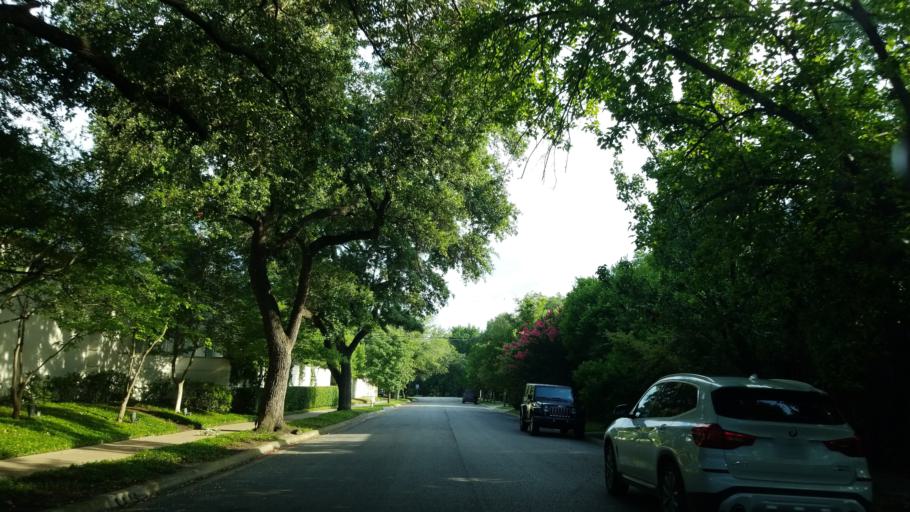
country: US
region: Texas
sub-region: Dallas County
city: Highland Park
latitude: 32.8337
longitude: -96.7947
